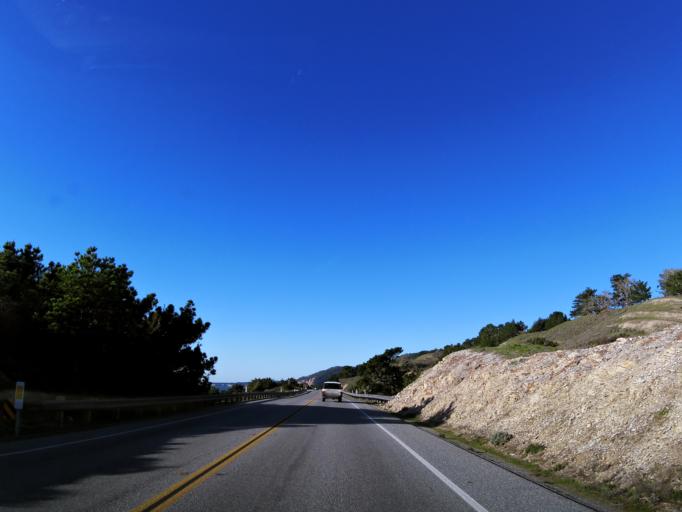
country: US
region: California
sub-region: Santa Cruz County
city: Bonny Doon
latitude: 37.0699
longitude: -122.2574
